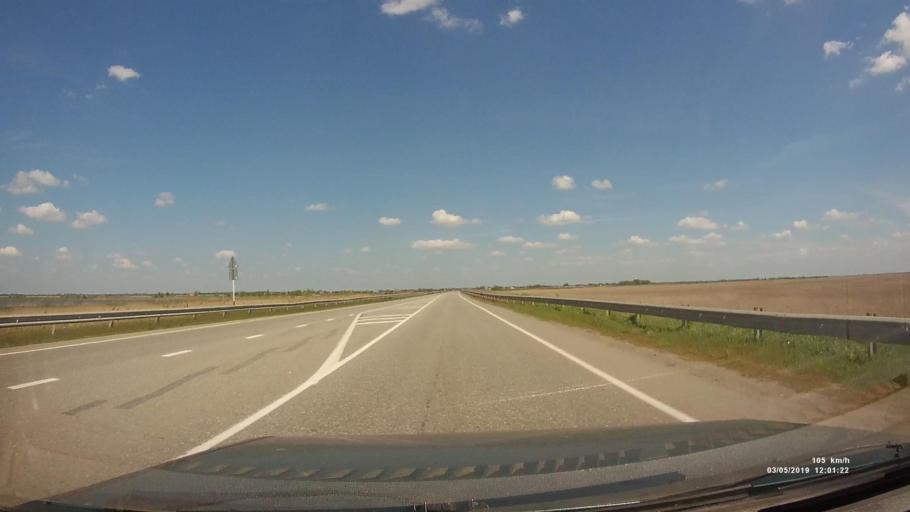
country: RU
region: Rostov
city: Bagayevskaya
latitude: 47.2616
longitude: 40.3499
